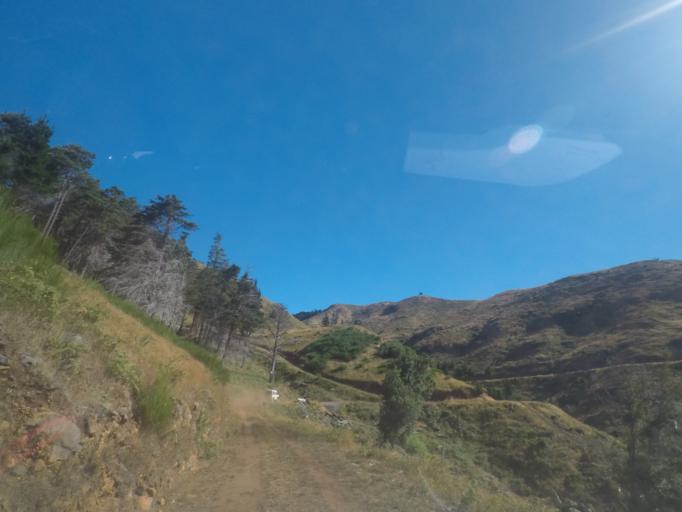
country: PT
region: Madeira
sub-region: Funchal
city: Nossa Senhora do Monte
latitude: 32.7075
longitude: -16.9029
